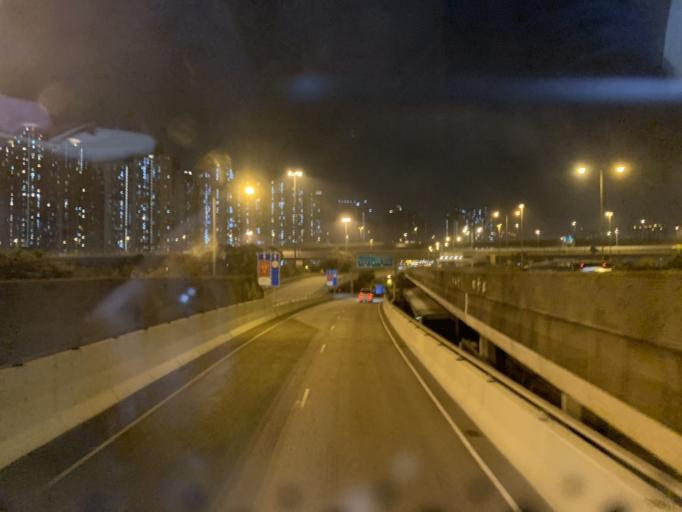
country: HK
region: Sham Shui Po
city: Sham Shui Po
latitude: 22.3327
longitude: 114.1405
